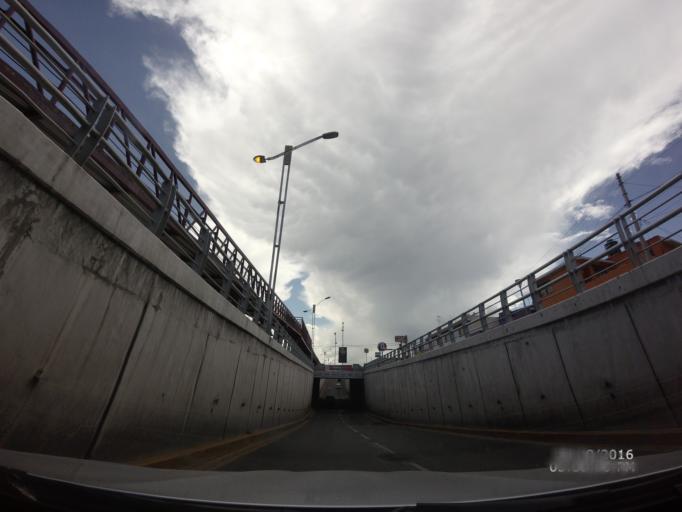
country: MX
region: Hidalgo
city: Pachuca de Soto
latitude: 20.1158
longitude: -98.7381
